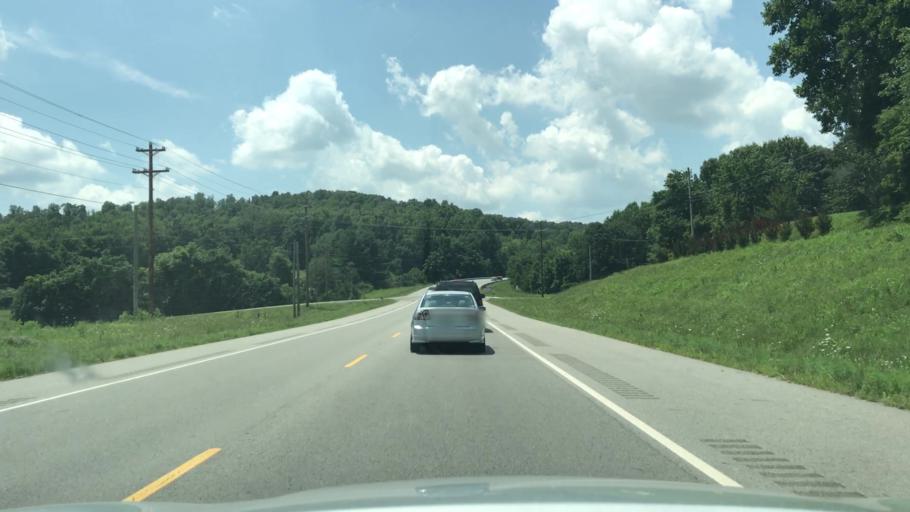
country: US
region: Tennessee
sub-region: Overton County
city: Livingston
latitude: 36.4056
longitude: -85.2911
